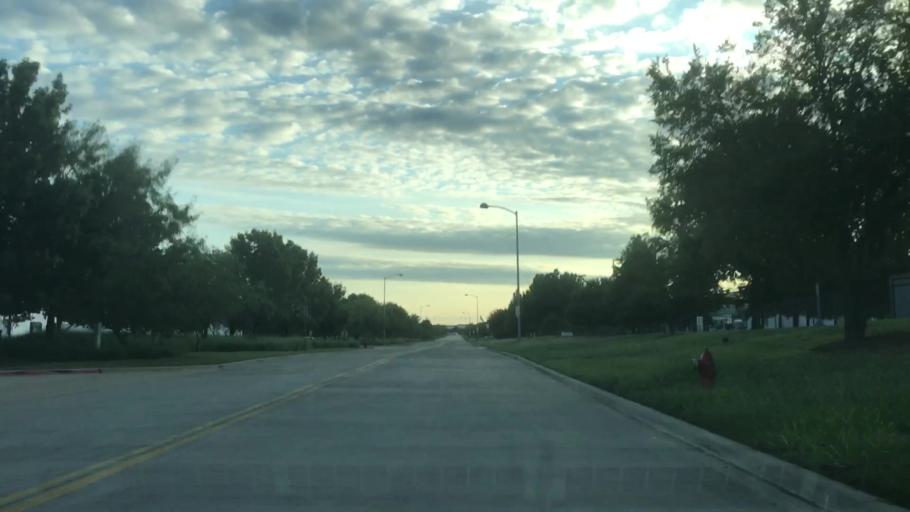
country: US
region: Texas
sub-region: Dallas County
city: Coppell
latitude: 32.9396
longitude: -97.0264
